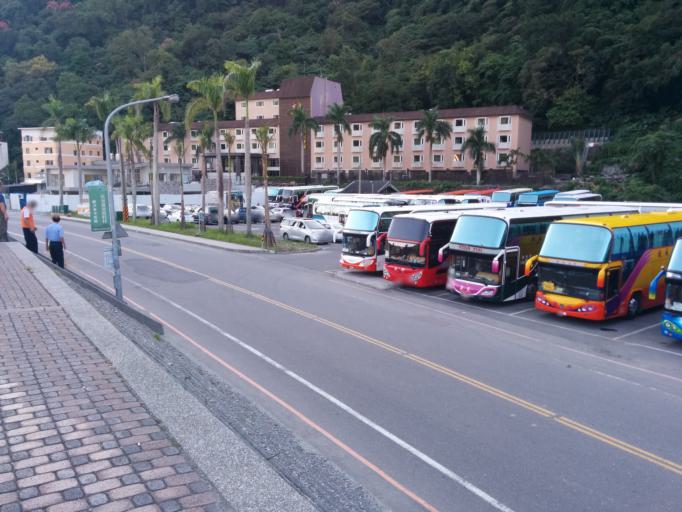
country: TW
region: Taiwan
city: Taitung City
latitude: 22.6928
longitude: 121.0197
